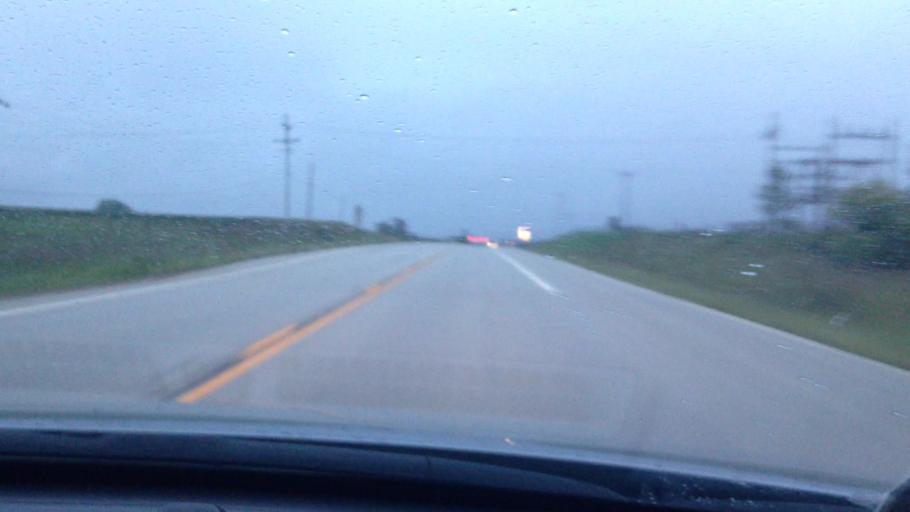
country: US
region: Kansas
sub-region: Brown County
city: Horton
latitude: 39.6675
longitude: -95.4912
